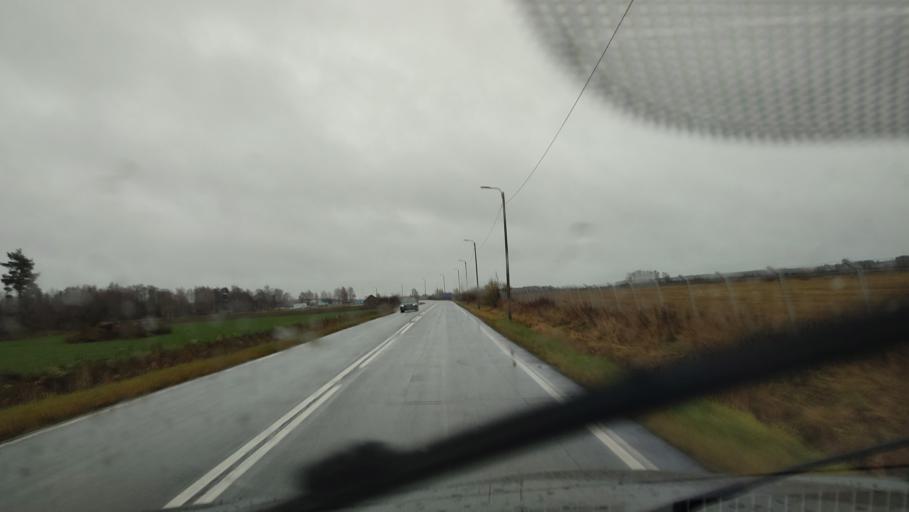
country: FI
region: Ostrobothnia
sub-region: Vaasa
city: Ristinummi
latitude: 63.0455
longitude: 21.7472
